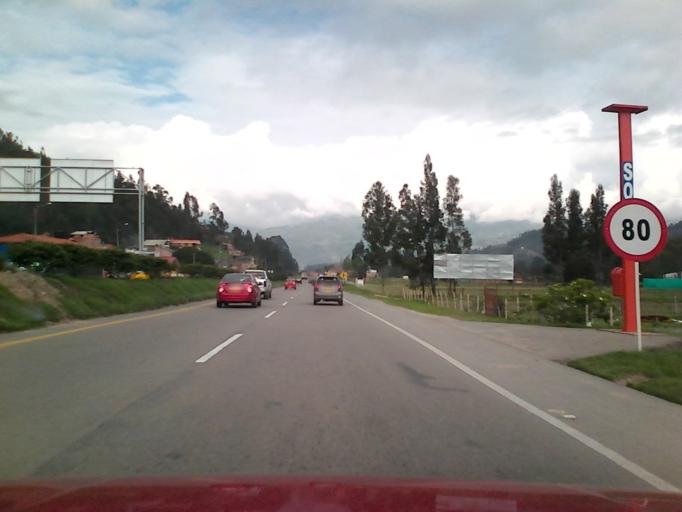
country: CO
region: Boyaca
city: Duitama
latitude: 5.7968
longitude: -72.9986
